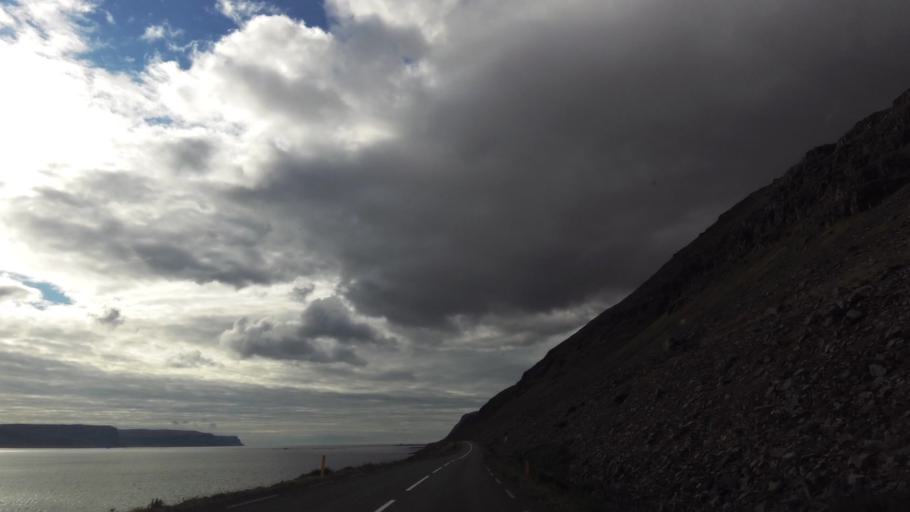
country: IS
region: West
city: Olafsvik
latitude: 65.5613
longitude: -23.9107
